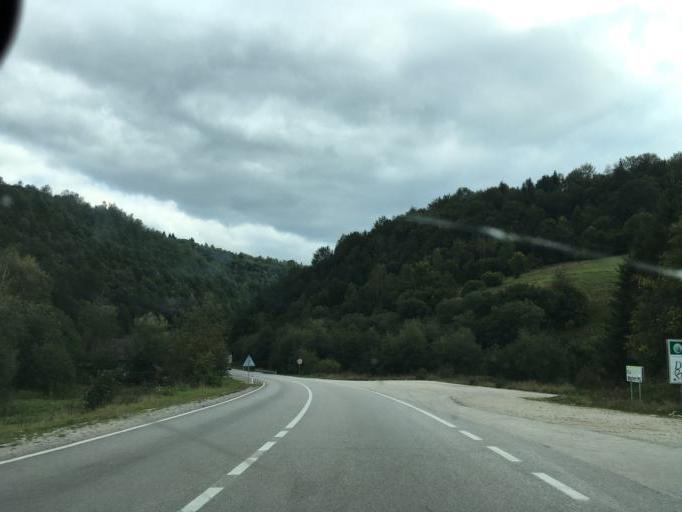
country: BA
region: Federation of Bosnia and Herzegovina
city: Novi Travnik
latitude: 44.1003
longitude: 17.5746
